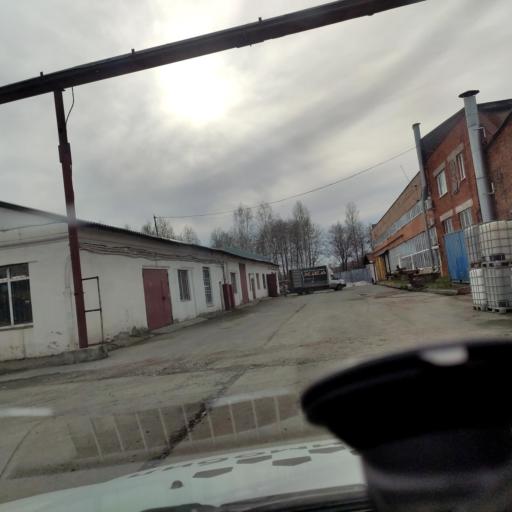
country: RU
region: Perm
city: Perm
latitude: 58.1054
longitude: 56.3481
